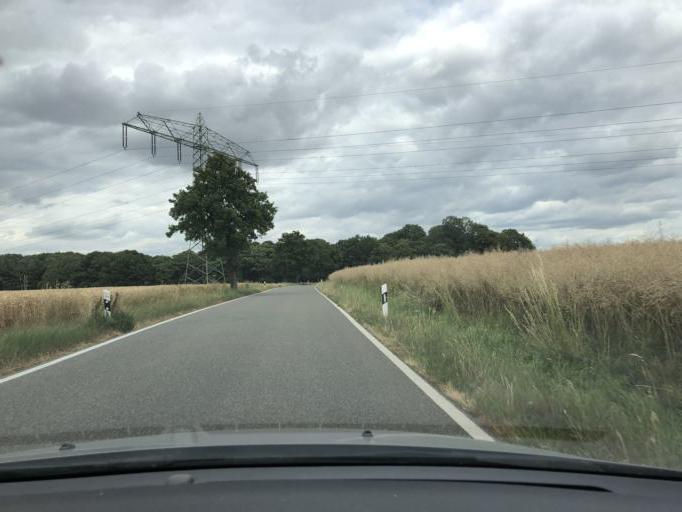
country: DE
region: Thuringia
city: Langenleuba-Niederhain
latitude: 51.0169
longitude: 12.6257
